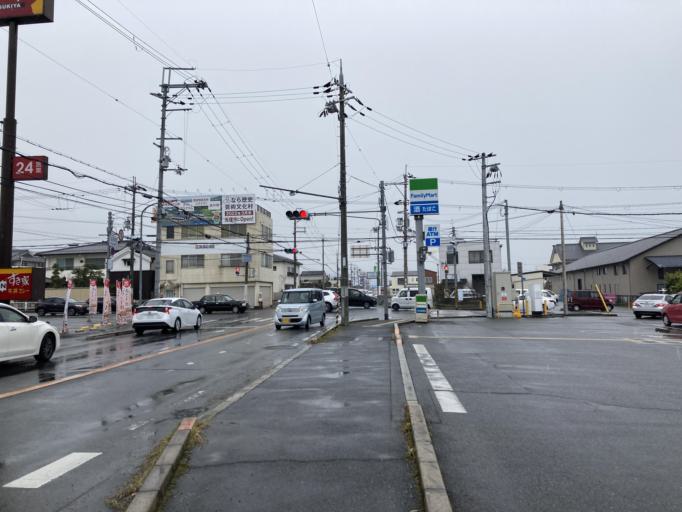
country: JP
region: Nara
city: Tenri
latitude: 34.5895
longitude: 135.8365
